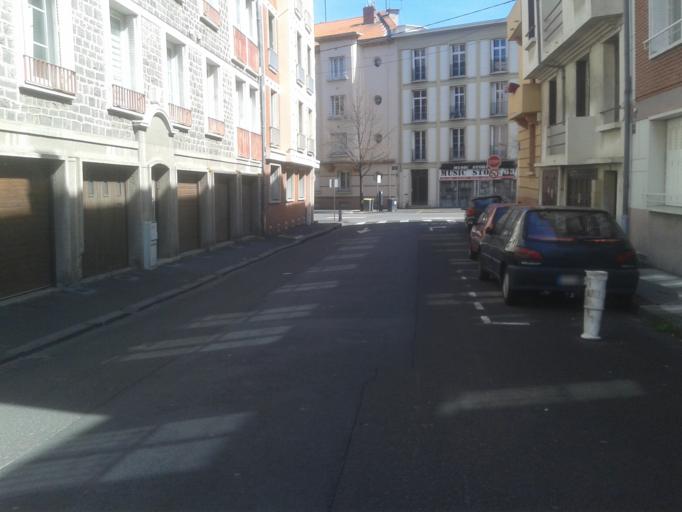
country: FR
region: Auvergne
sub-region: Departement du Puy-de-Dome
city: Chamalieres
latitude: 45.7699
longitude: 3.0756
